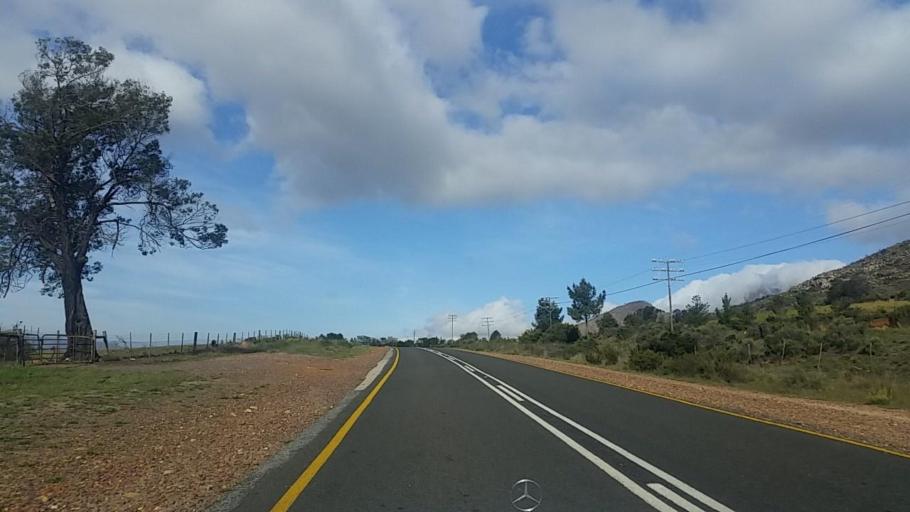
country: ZA
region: Western Cape
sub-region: Eden District Municipality
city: George
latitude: -33.8343
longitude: 22.4463
